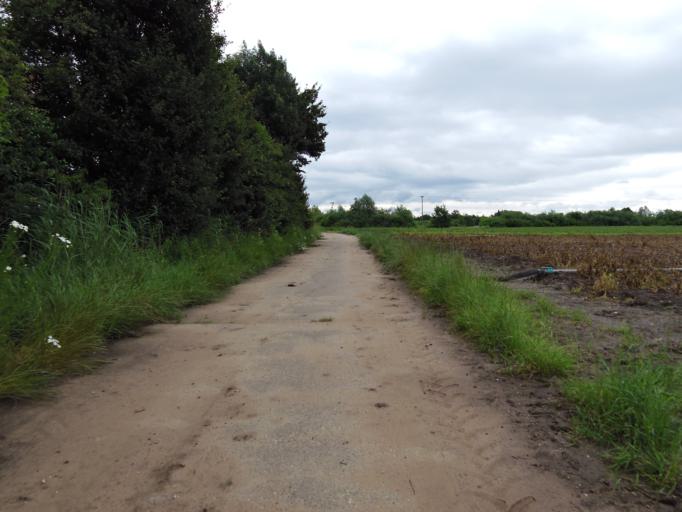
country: DE
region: Rheinland-Pfalz
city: Heuchelheim bei Frankenthal
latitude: 49.5609
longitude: 8.3018
